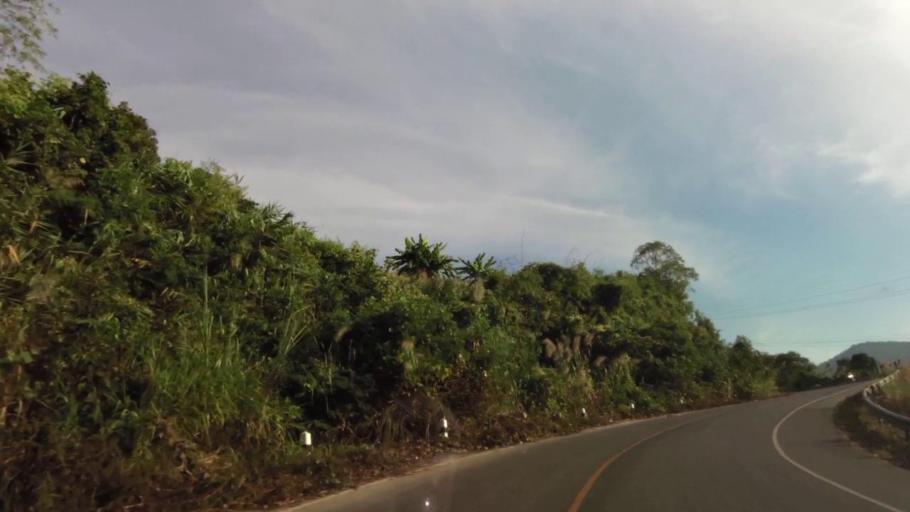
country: TH
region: Chiang Rai
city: Khun Tan
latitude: 19.8658
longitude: 100.4177
